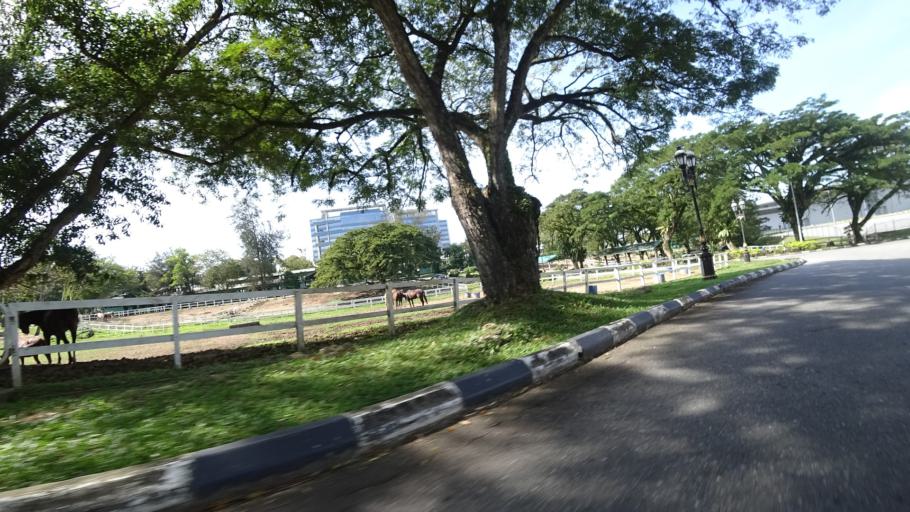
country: BN
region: Brunei and Muara
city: Bandar Seri Begawan
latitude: 4.9478
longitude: 114.8338
